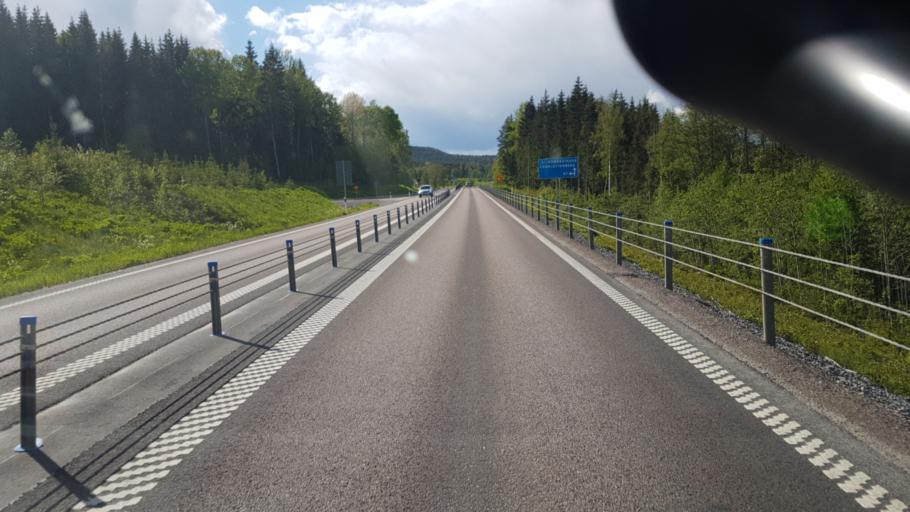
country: SE
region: Vaermland
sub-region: Eda Kommun
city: Amotfors
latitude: 59.7855
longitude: 12.3531
